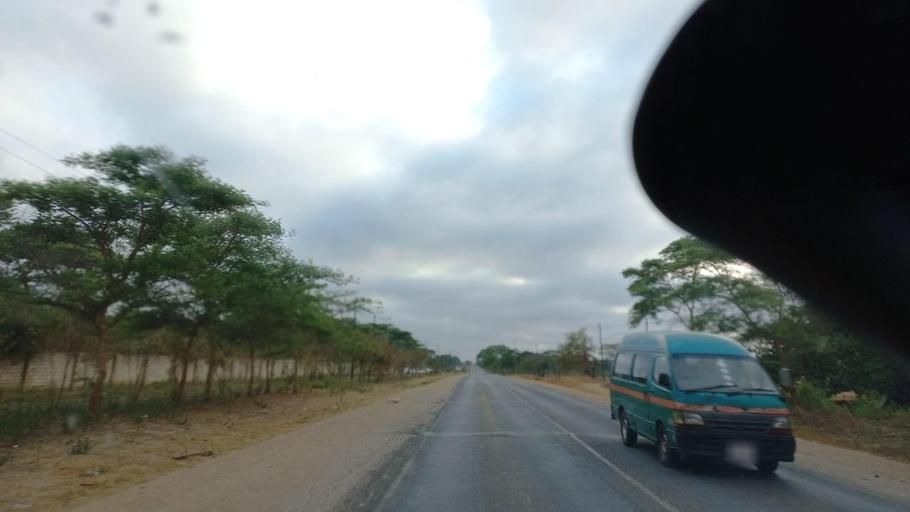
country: ZM
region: Lusaka
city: Chongwe
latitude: -15.3477
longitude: 28.5034
